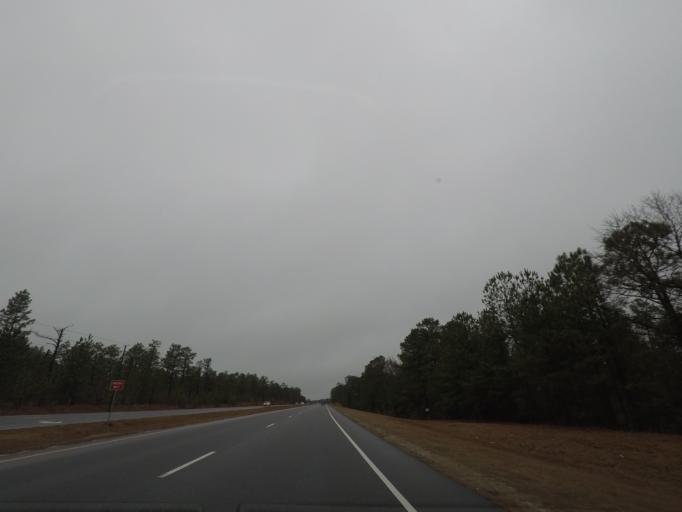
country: US
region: North Carolina
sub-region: Cumberland County
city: Spring Lake
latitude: 35.2364
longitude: -79.0201
